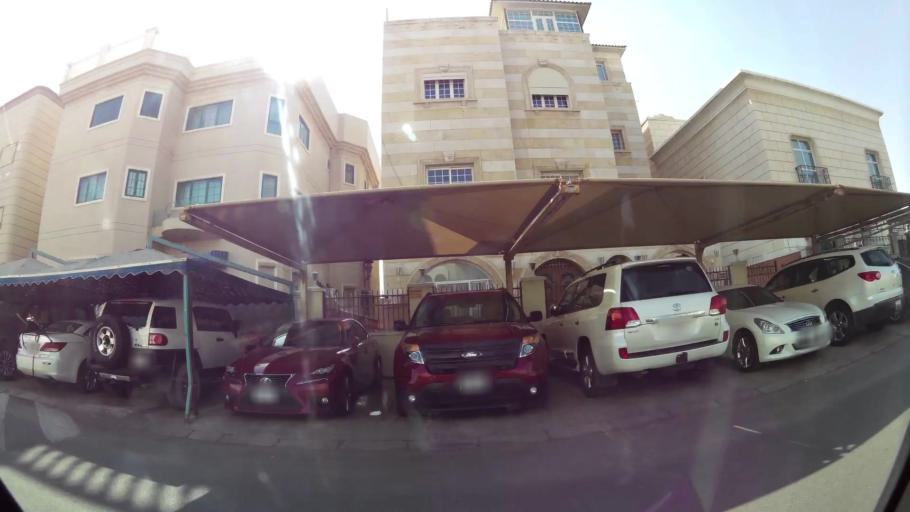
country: KW
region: Muhafazat Hawalli
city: Salwa
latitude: 29.2780
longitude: 48.0811
